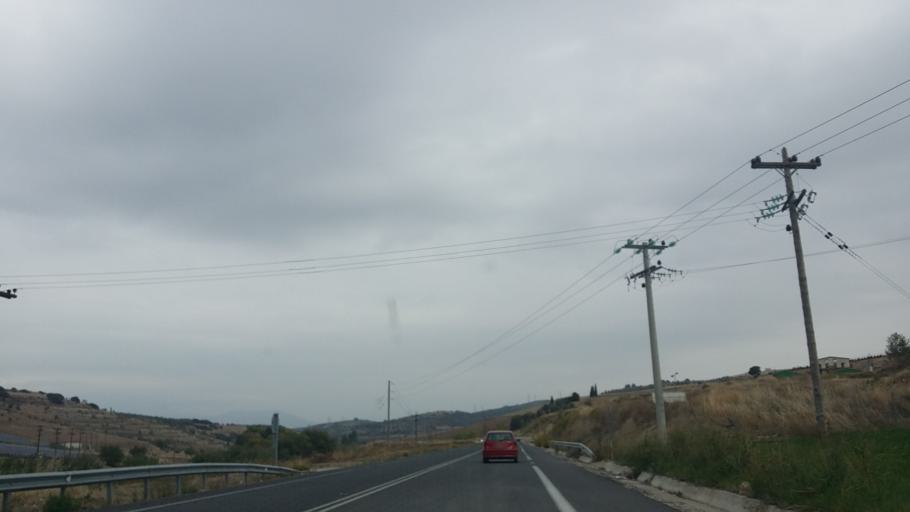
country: GR
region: Central Greece
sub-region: Nomos Voiotias
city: Vagia
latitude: 38.3030
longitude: 23.2393
